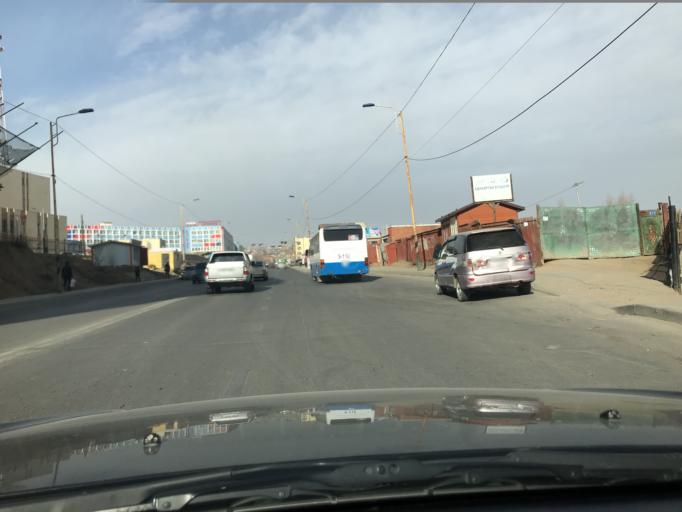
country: MN
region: Ulaanbaatar
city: Ulaanbaatar
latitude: 47.9269
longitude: 106.8936
